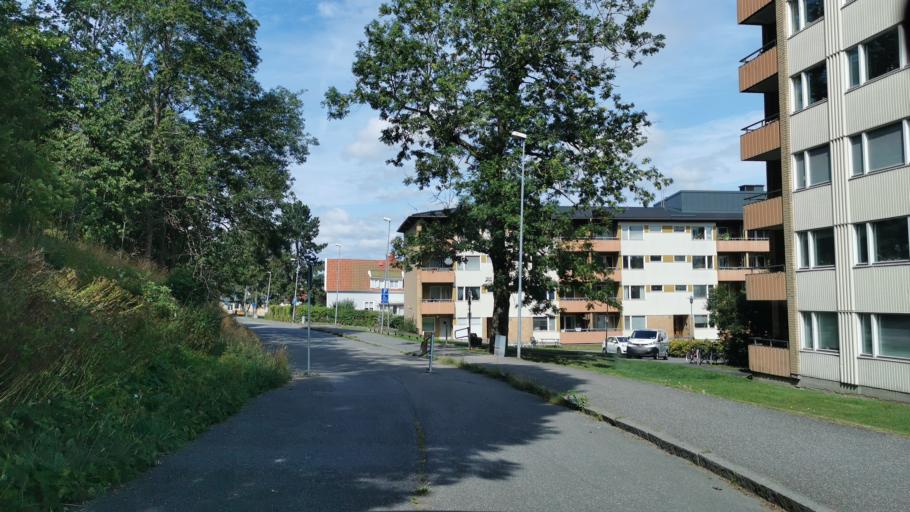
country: SE
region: Vaestra Goetaland
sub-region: Molndal
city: Moelndal
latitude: 57.6720
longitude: 12.0051
